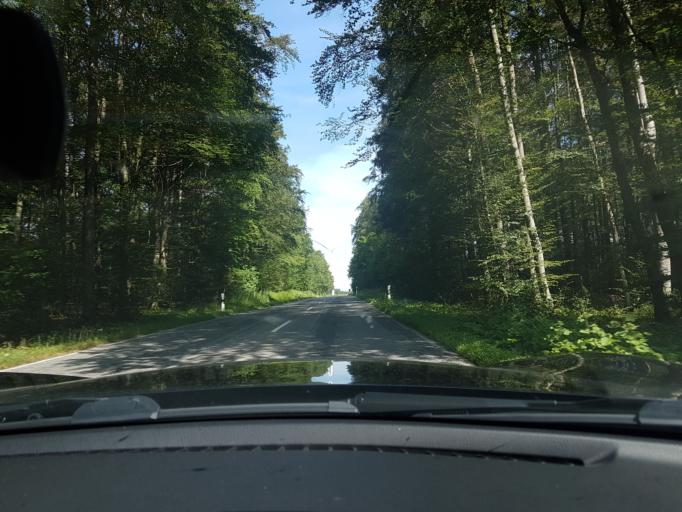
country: DE
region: Baden-Wuerttemberg
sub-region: Karlsruhe Region
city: Seckach
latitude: 49.4478
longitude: 9.2744
